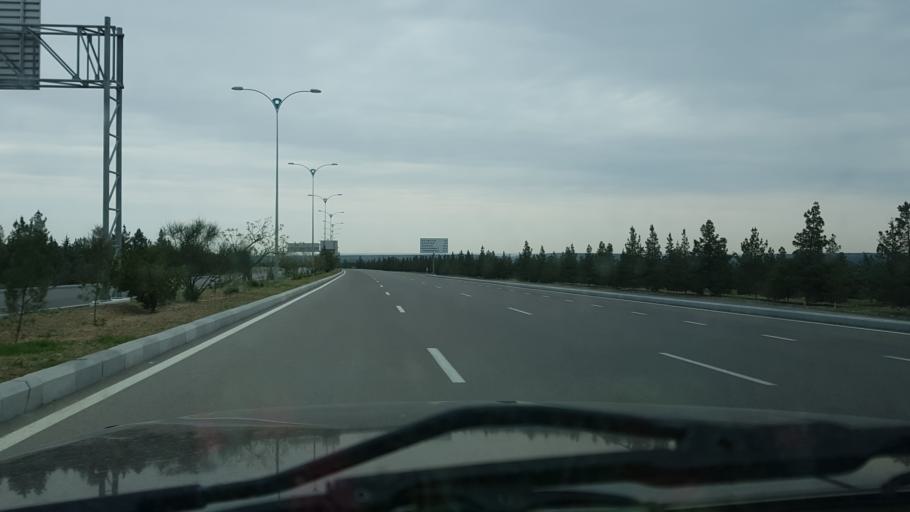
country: TM
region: Ahal
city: Ashgabat
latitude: 37.9013
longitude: 58.2521
